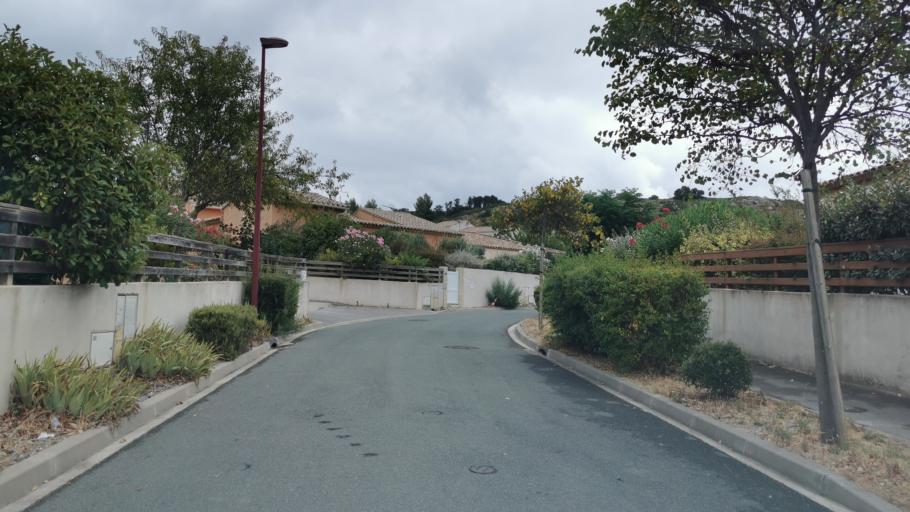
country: FR
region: Languedoc-Roussillon
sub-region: Departement de l'Aude
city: Nevian
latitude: 43.1898
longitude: 2.9161
